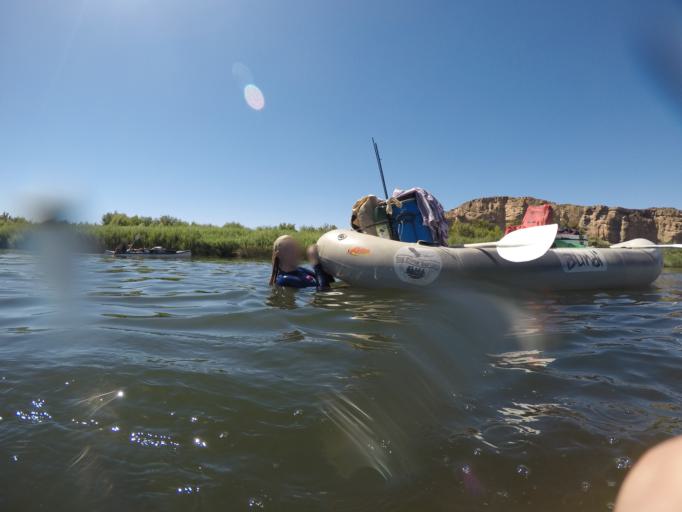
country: ZA
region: Northern Cape
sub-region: Namakwa District Municipality
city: Port Nolloth
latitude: -28.6991
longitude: 17.5480
